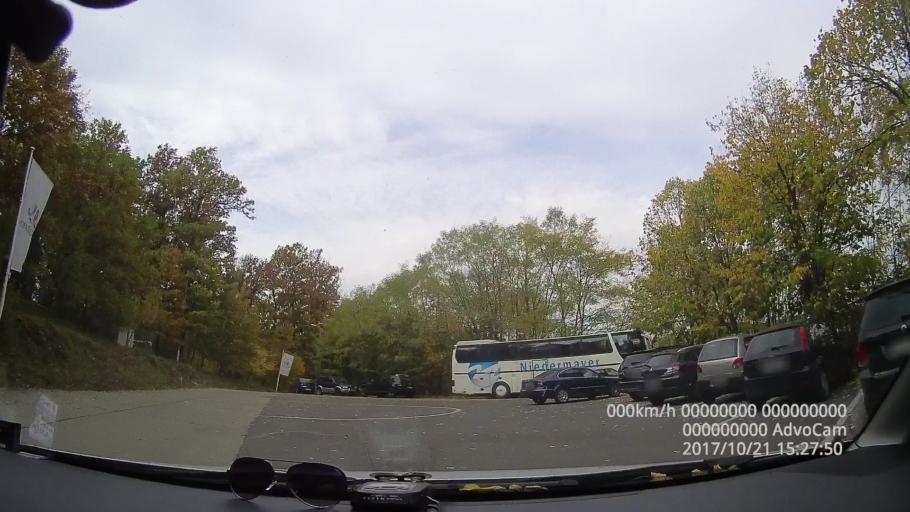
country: RO
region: Hunedoara
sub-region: Municipiul Deva
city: Deva
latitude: 45.8730
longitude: 22.9182
